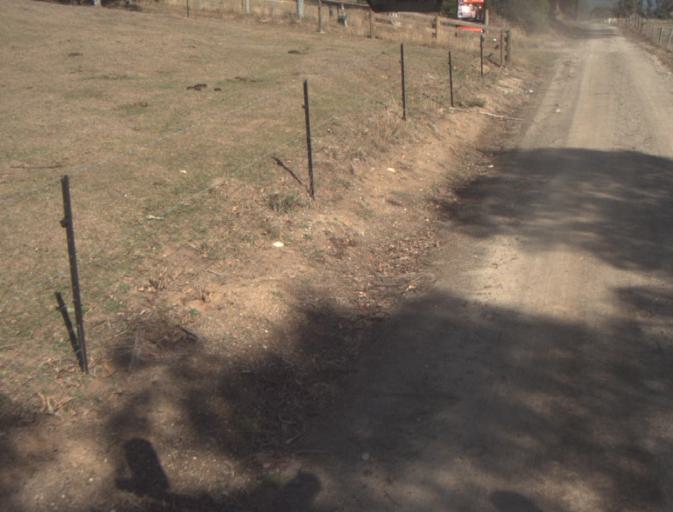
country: AU
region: Tasmania
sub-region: Launceston
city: Mayfield
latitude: -41.2202
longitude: 147.2392
